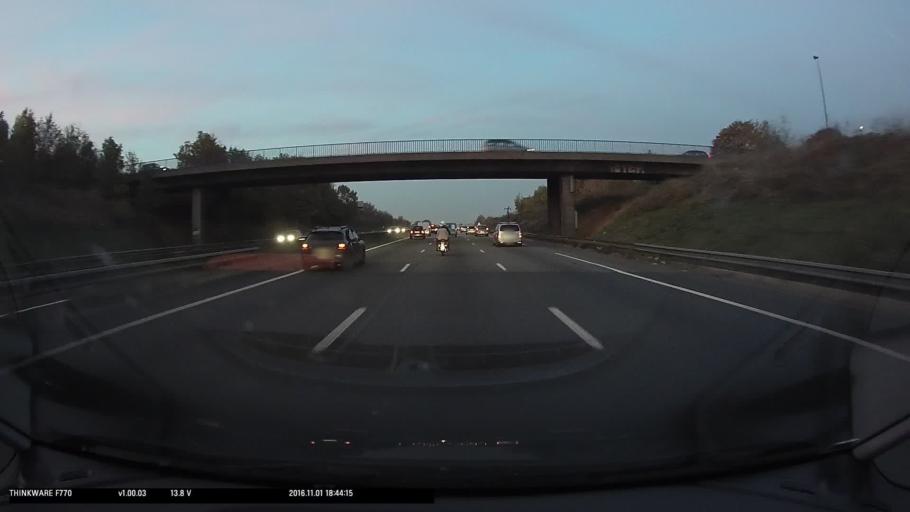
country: FR
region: Ile-de-France
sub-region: Departement de l'Essonne
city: Chilly-Mazarin
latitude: 48.7116
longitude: 2.3079
